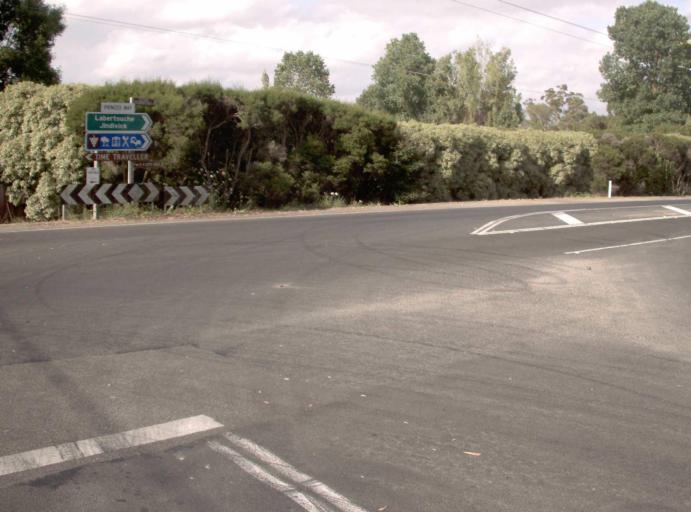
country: AU
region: Victoria
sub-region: Cardinia
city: Bunyip
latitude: -38.0819
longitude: 145.7783
